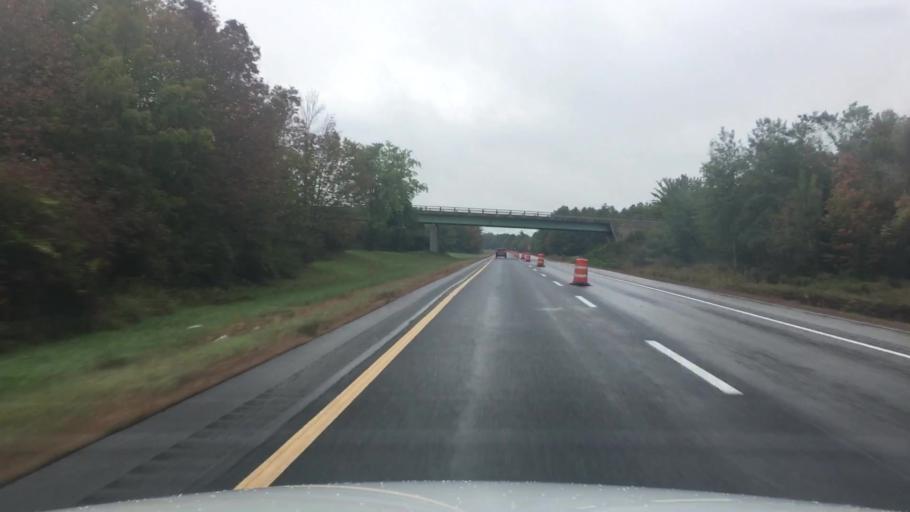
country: US
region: Maine
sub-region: Sagadahoc County
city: Richmond
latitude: 44.1126
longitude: -69.8584
